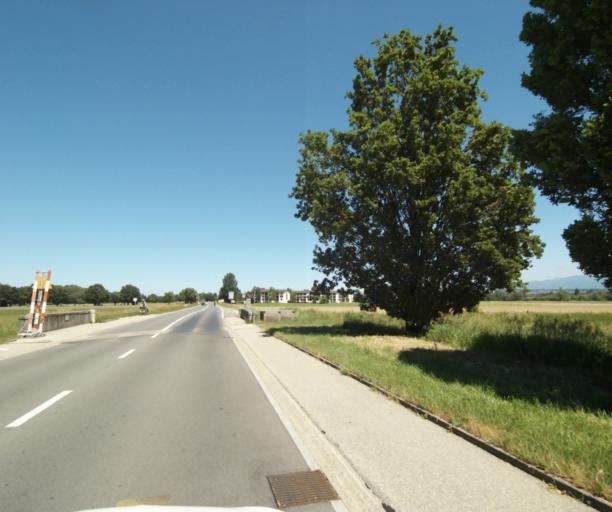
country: FR
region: Rhone-Alpes
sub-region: Departement de la Haute-Savoie
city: Veigy-Foncenex
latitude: 46.2726
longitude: 6.2426
